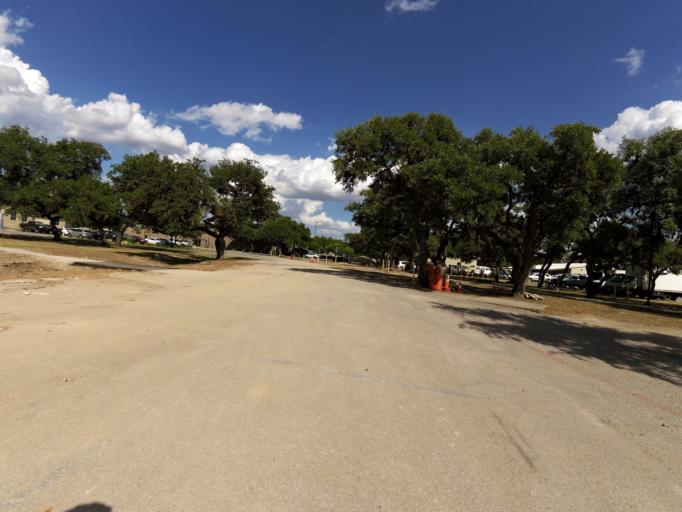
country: US
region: Texas
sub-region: Bexar County
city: Helotes
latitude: 29.5834
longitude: -98.6300
